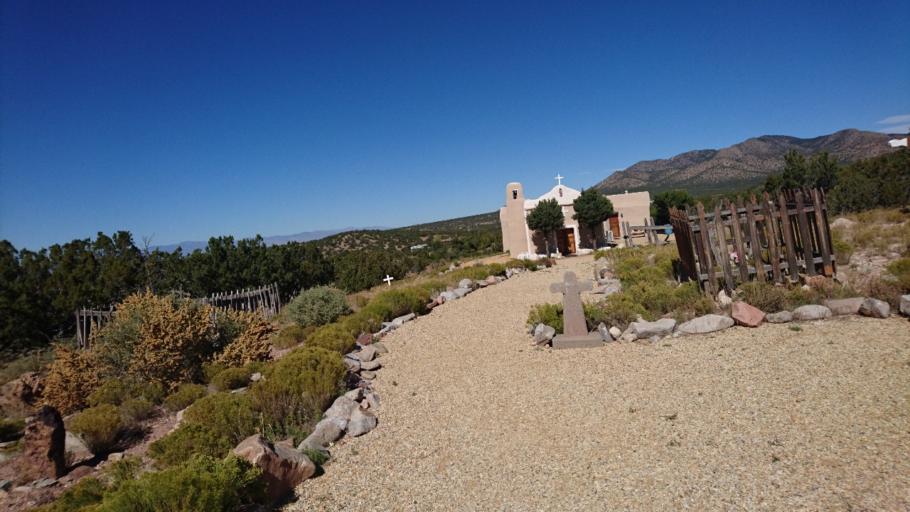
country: US
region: New Mexico
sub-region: Bernalillo County
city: Sandia Knolls
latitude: 35.2691
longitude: -106.2133
